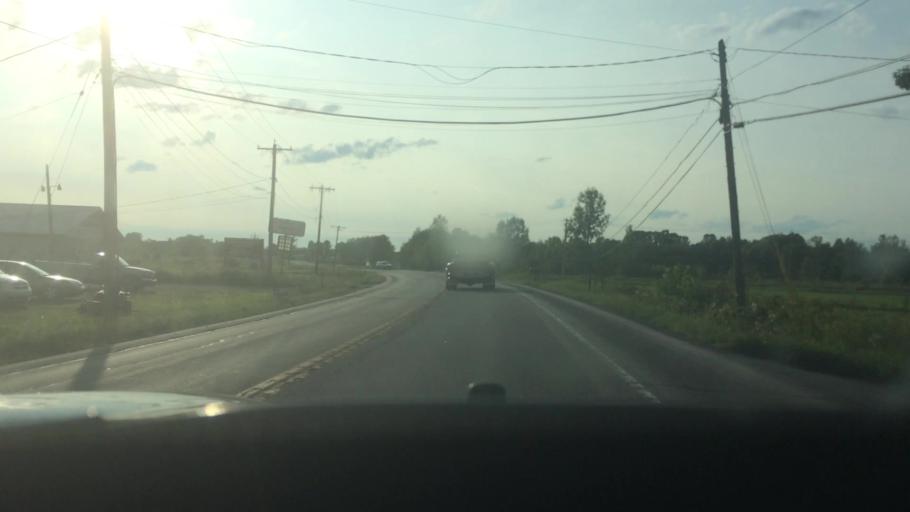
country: US
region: New York
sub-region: St. Lawrence County
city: Ogdensburg
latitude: 44.6877
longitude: -75.4567
